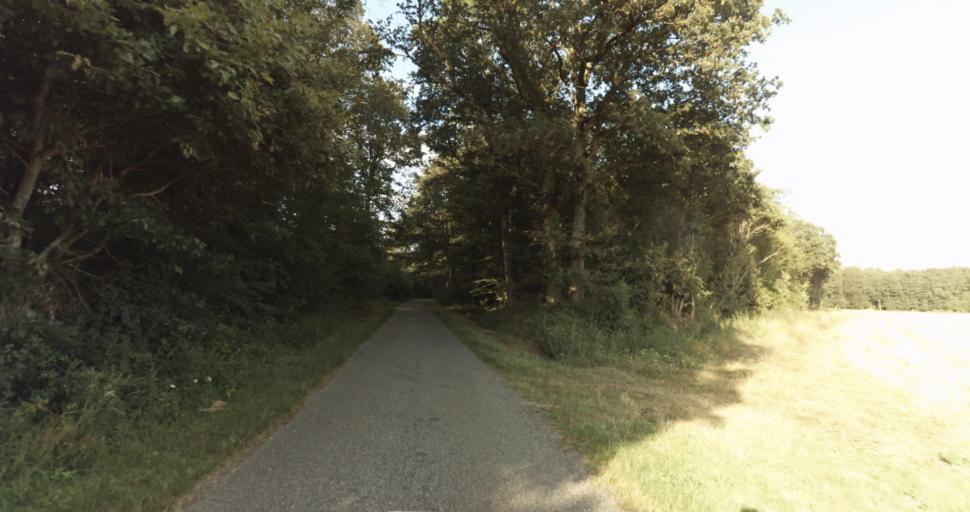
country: FR
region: Haute-Normandie
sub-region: Departement de l'Eure
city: Marcilly-sur-Eure
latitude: 48.8691
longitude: 1.2995
